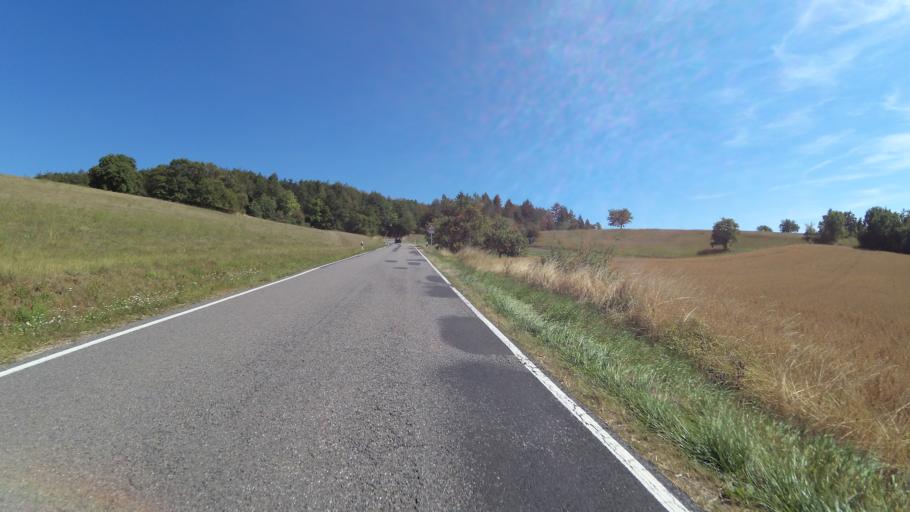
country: DE
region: Rheinland-Pfalz
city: Hornbach
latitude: 49.1655
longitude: 7.3169
